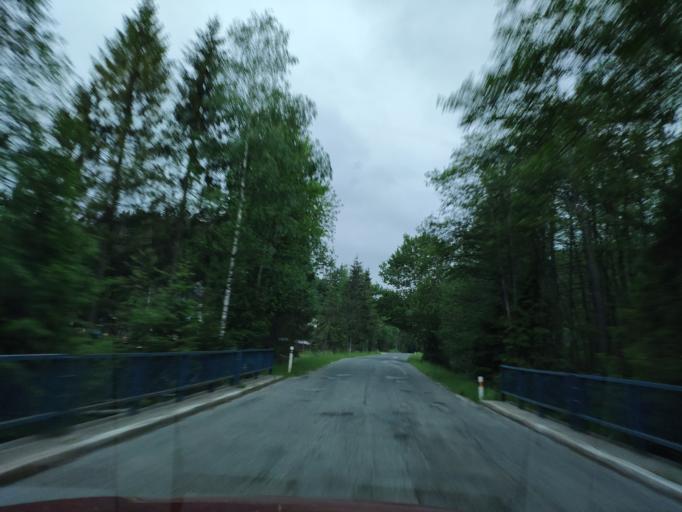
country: SK
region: Kosicky
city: Roznava
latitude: 48.7141
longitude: 20.7064
